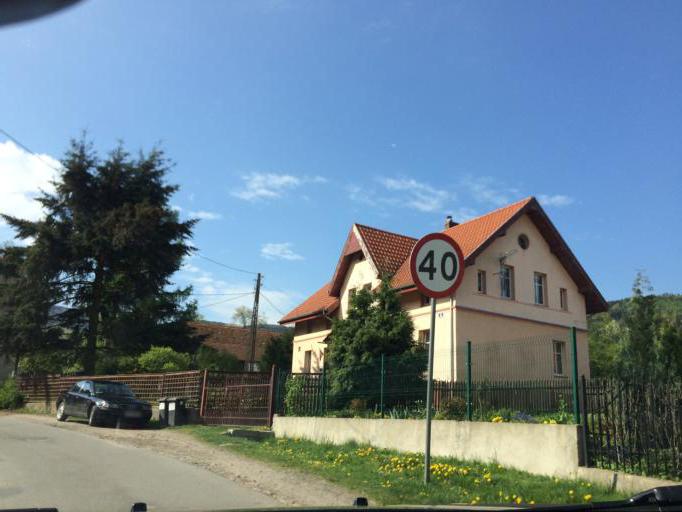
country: PL
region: Lower Silesian Voivodeship
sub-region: Powiat dzierzoniowski
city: Pieszyce
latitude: 50.6786
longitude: 16.5431
